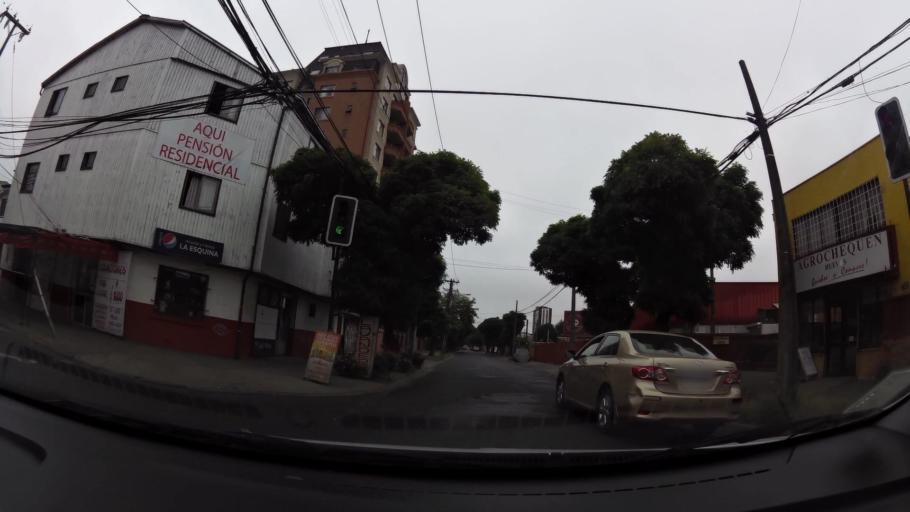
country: CL
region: Biobio
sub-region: Provincia de Concepcion
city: Concepcion
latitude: -36.8149
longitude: -73.0349
